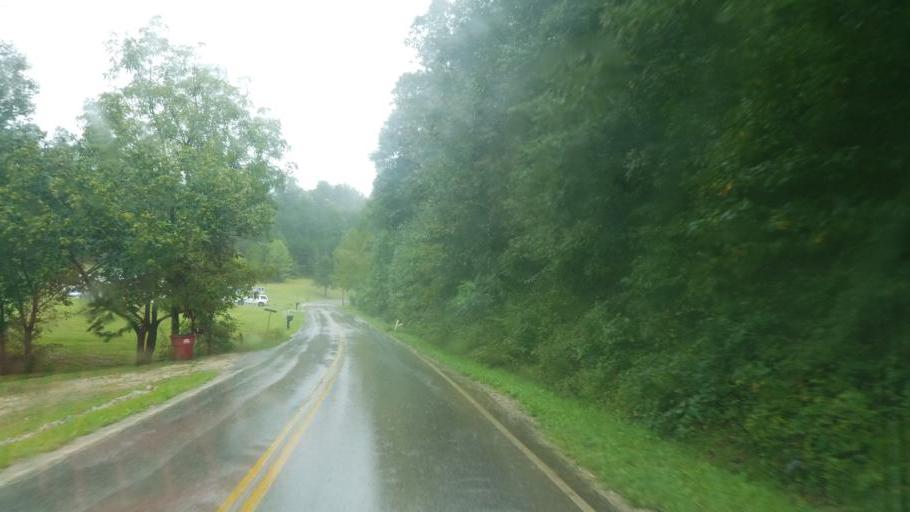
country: US
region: Ohio
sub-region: Scioto County
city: Franklin Furnace
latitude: 38.6444
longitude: -82.9299
